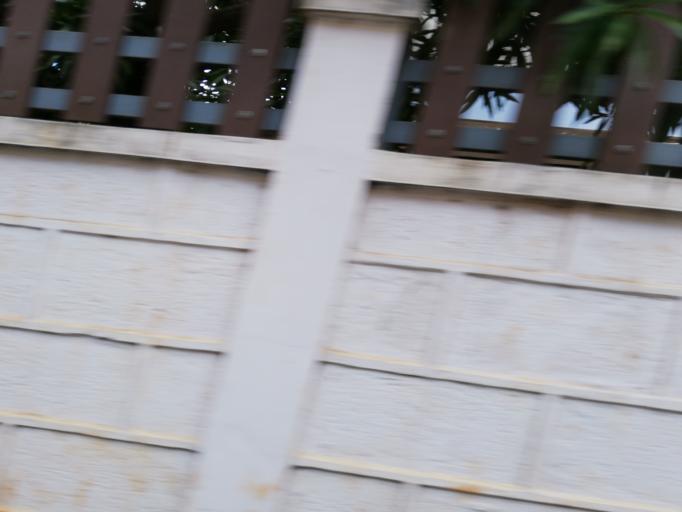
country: MU
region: Moka
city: Pailles
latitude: -20.2043
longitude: 57.4710
